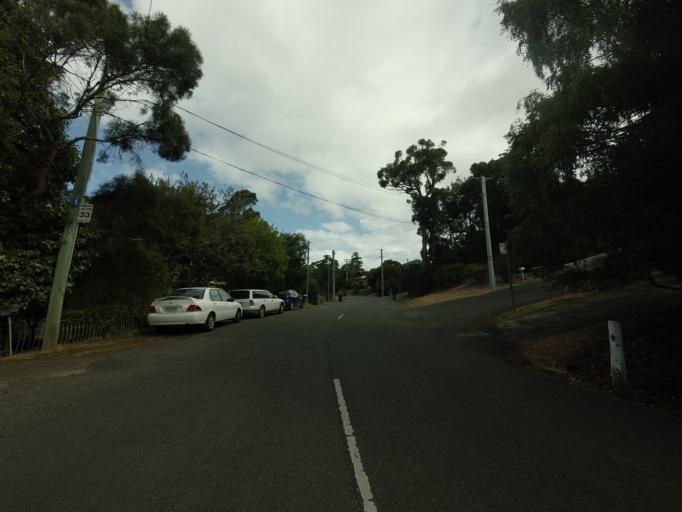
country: AU
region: Tasmania
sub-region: Hobart
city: Dynnyrne
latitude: -42.9020
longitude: 147.2705
